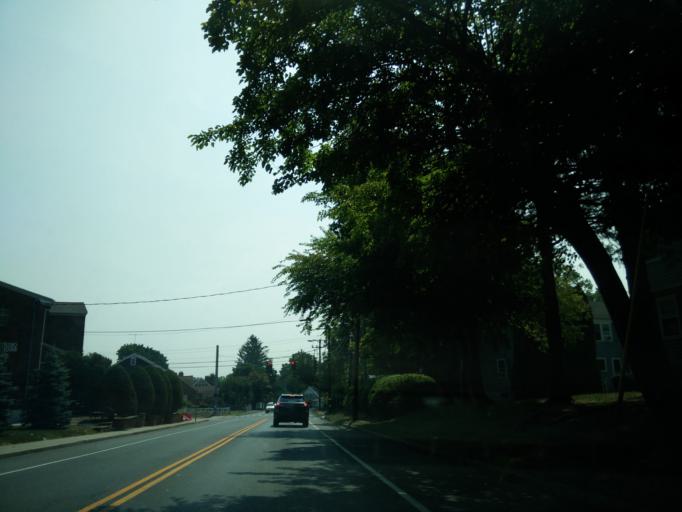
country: US
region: Connecticut
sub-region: Fairfield County
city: Bridgeport
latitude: 41.1737
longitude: -73.2369
